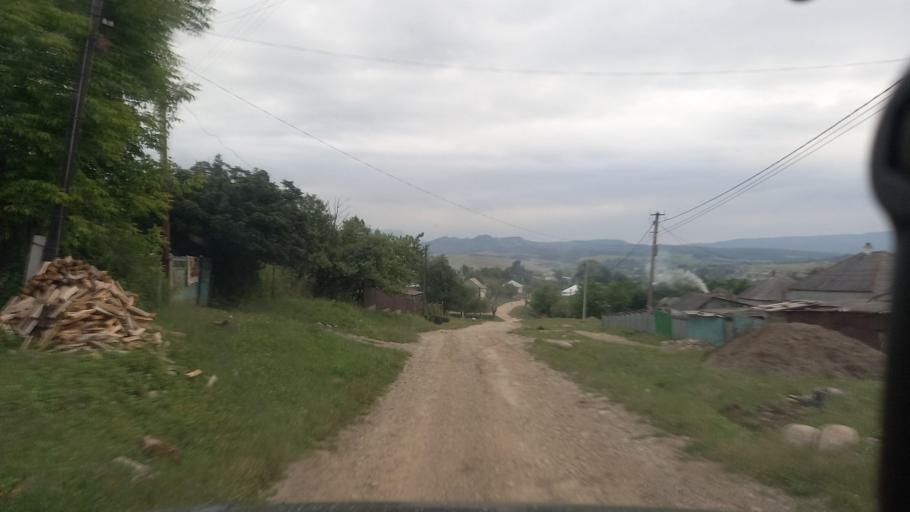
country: RU
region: Karachayevo-Cherkesiya
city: Pregradnaya
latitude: 43.9513
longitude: 41.1780
